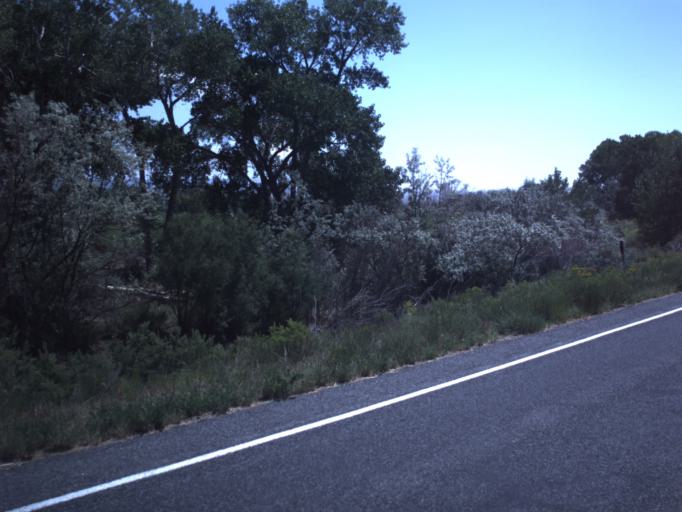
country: US
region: Utah
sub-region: Emery County
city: Orangeville
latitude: 39.2162
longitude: -111.0653
